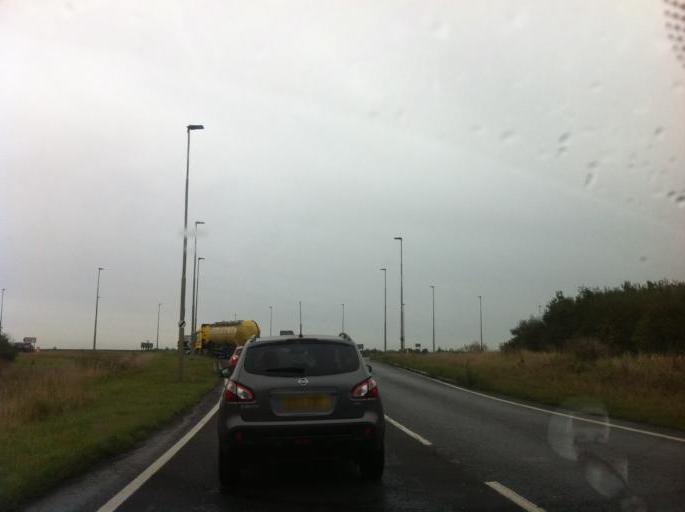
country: GB
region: England
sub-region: Peterborough
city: Newborough
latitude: 52.6367
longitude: -0.1960
